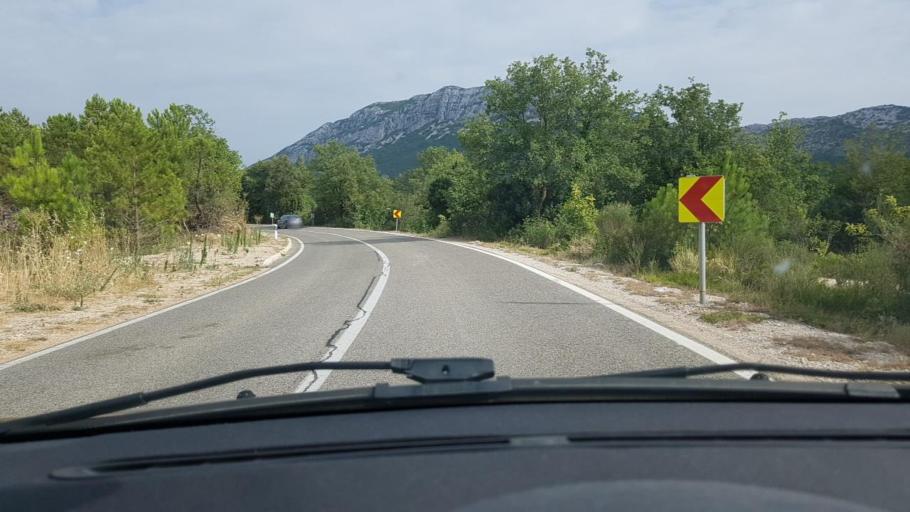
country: BA
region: Federation of Bosnia and Herzegovina
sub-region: Hercegovacko-Bosanski Kanton
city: Neum
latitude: 42.8752
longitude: 17.5199
